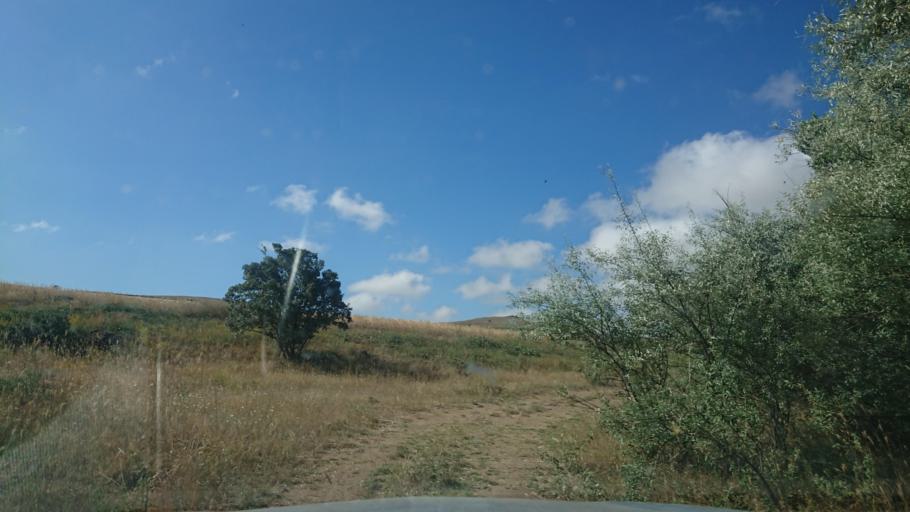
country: TR
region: Aksaray
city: Agacoren
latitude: 38.8466
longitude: 33.9306
